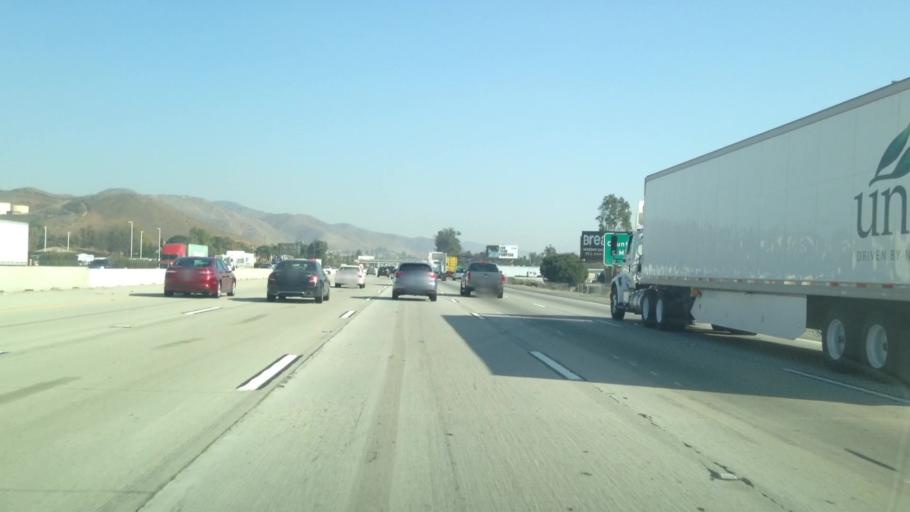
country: US
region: California
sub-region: Riverside County
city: Mira Loma
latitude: 34.0182
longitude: -117.5170
